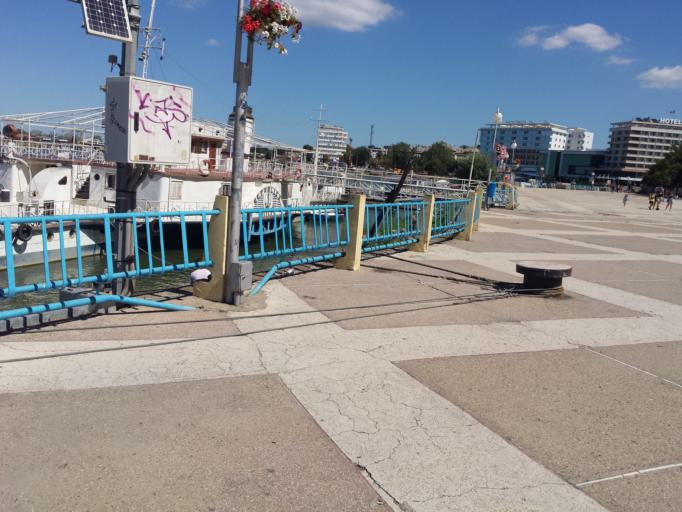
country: RO
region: Tulcea
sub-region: Municipiul Tulcea
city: Tulcea
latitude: 45.1801
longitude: 28.7997
